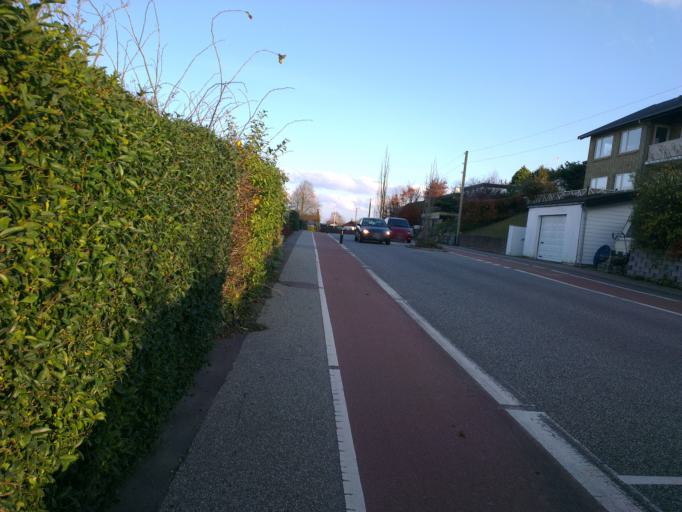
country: DK
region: Capital Region
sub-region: Frederikssund Kommune
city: Jaegerspris
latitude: 55.8525
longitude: 11.9928
